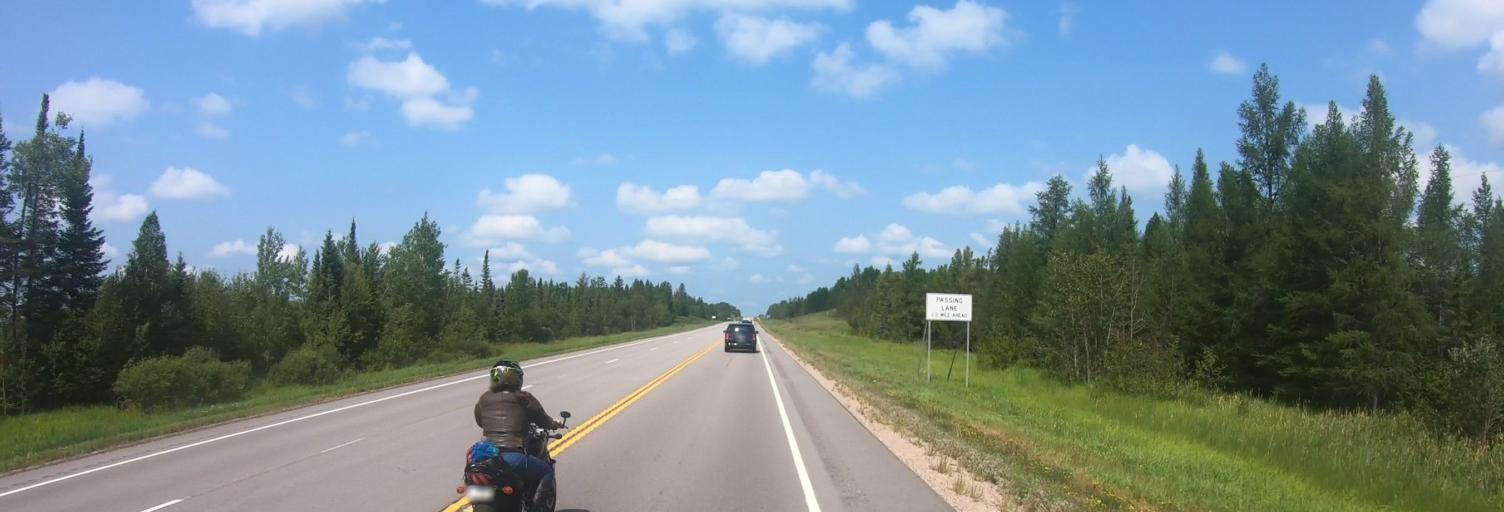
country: US
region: Minnesota
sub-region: Saint Louis County
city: Mountain Iron
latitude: 47.9051
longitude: -92.7940
